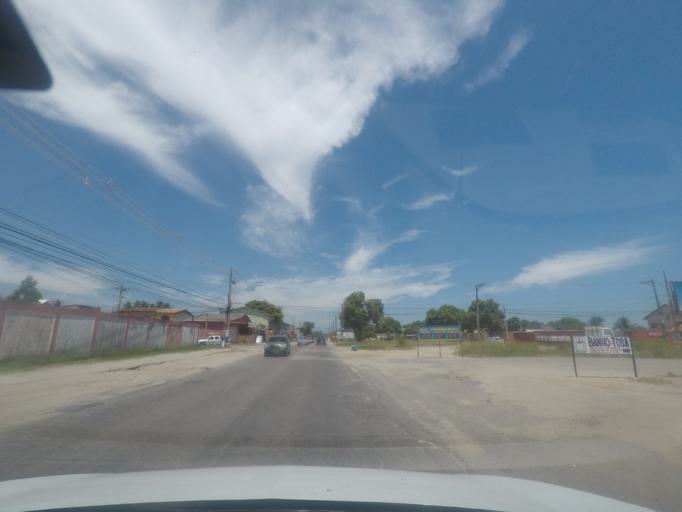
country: BR
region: Rio de Janeiro
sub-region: Itaguai
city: Itaguai
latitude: -22.9796
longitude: -43.6680
